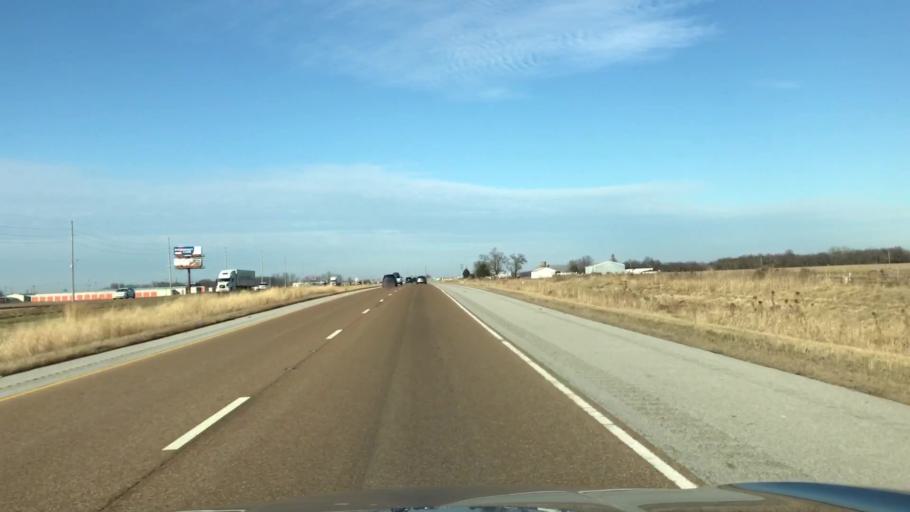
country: US
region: Illinois
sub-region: Macoupin County
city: Staunton
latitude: 39.0015
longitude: -89.7496
